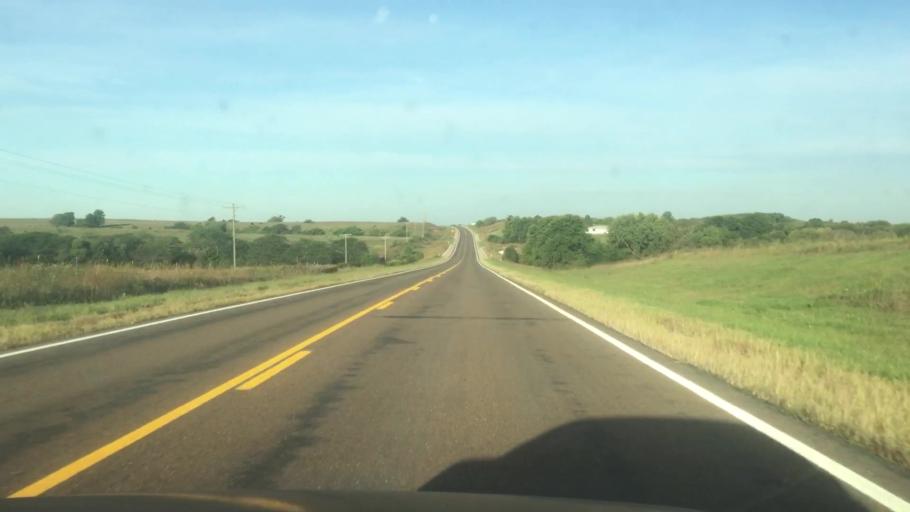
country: US
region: Nebraska
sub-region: Gage County
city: Wymore
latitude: 40.0457
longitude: -96.7560
